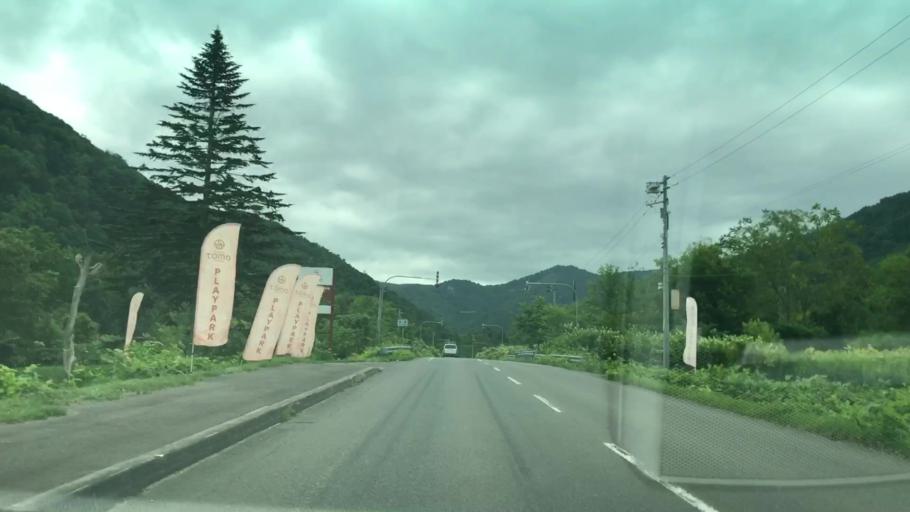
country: JP
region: Hokkaido
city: Yoichi
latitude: 43.0281
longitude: 140.8661
